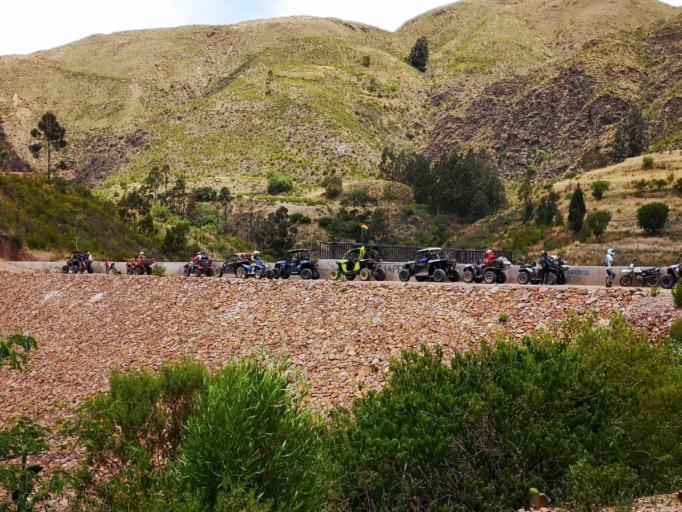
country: BO
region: Cochabamba
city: Capinota
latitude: -17.6838
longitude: -66.1671
